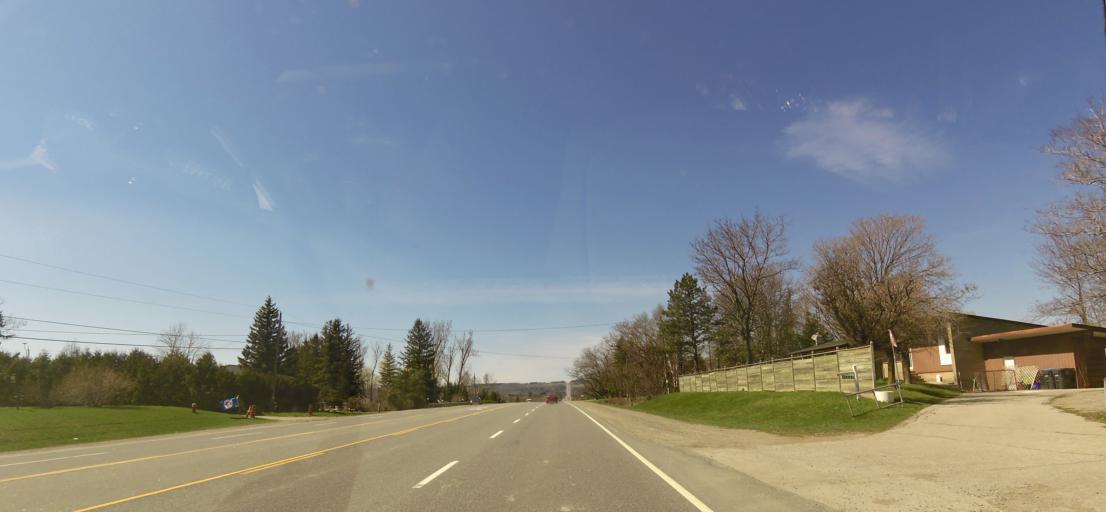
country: CA
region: Ontario
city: Brampton
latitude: 43.8044
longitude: -79.9205
